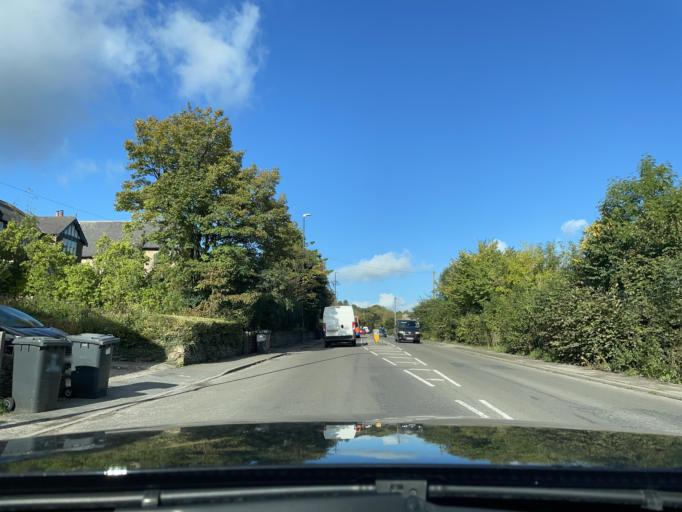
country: GB
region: England
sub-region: Derbyshire
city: New Mills
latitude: 53.3526
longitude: -1.9960
